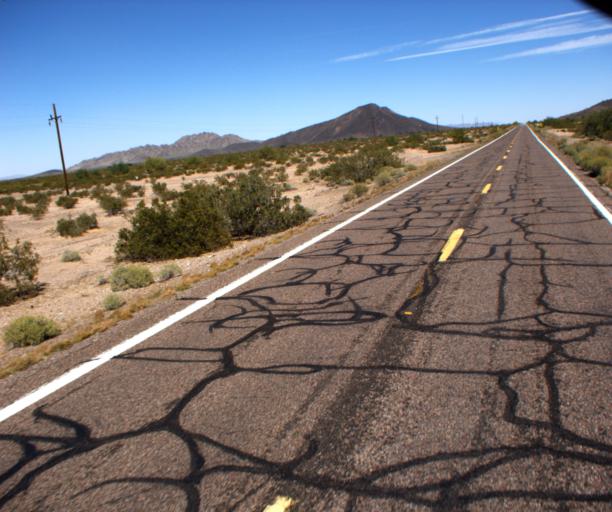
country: US
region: Arizona
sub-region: Maricopa County
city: Gila Bend
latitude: 32.7313
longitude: -112.8350
